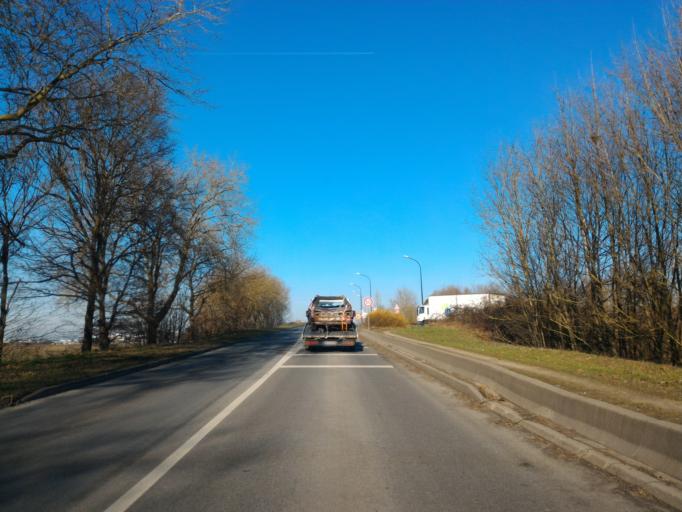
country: FR
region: Ile-de-France
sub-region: Departement de l'Essonne
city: Le Coudray-Montceaux
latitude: 48.5594
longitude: 2.4839
